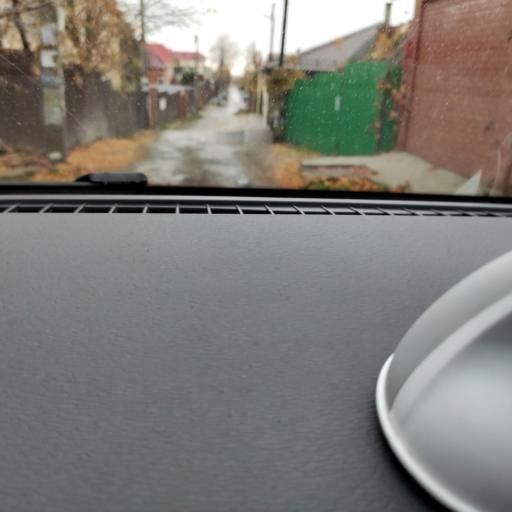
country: RU
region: Samara
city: Samara
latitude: 53.2682
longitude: 50.2118
